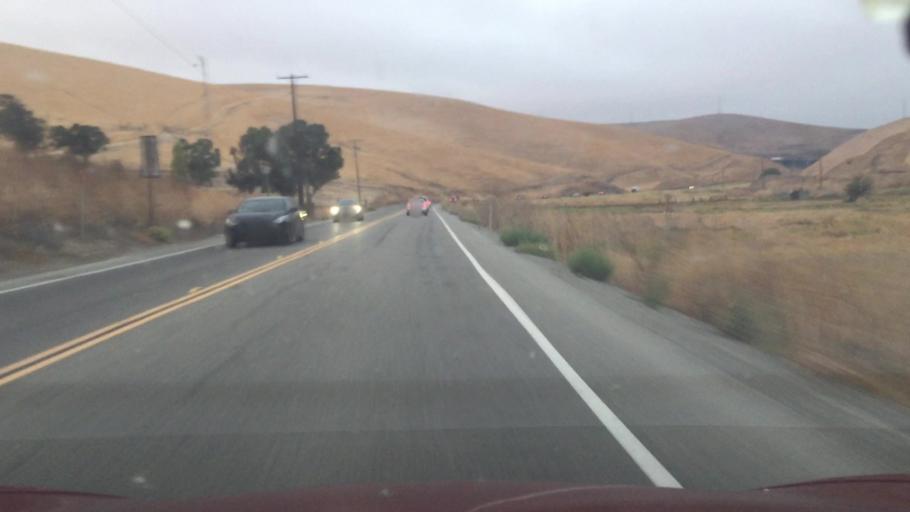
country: US
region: California
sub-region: Alameda County
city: Livermore
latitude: 37.7368
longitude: -121.6703
